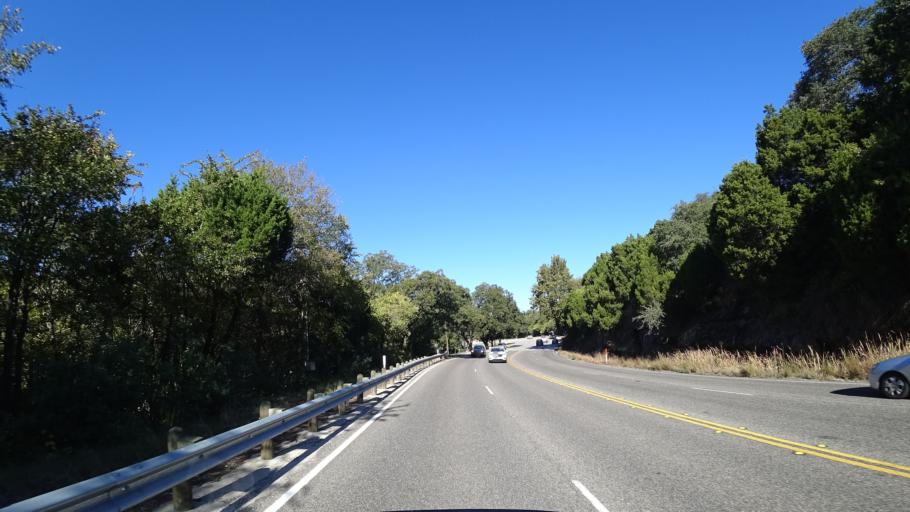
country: US
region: Texas
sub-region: Travis County
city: West Lake Hills
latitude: 30.3569
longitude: -97.7846
